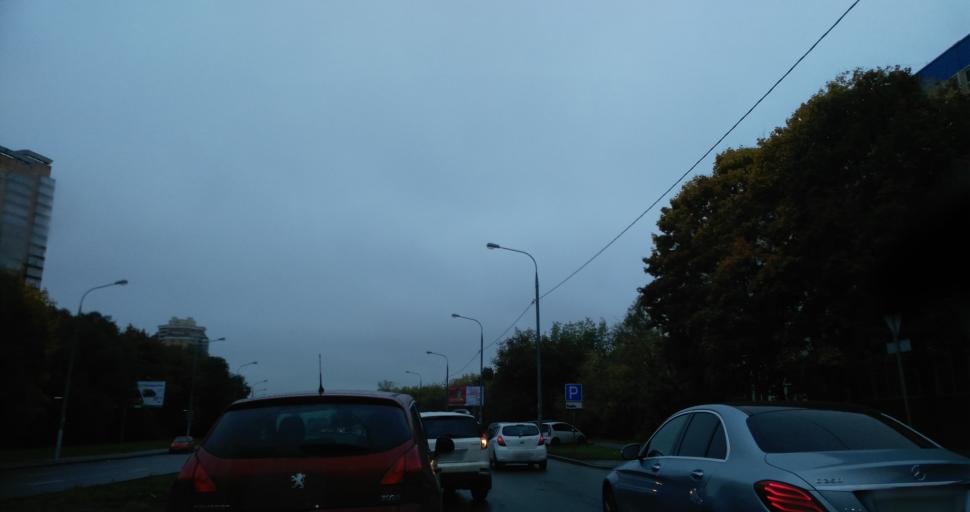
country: RU
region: Moskovskaya
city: Levoberezhnyy
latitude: 55.8612
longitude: 37.4868
